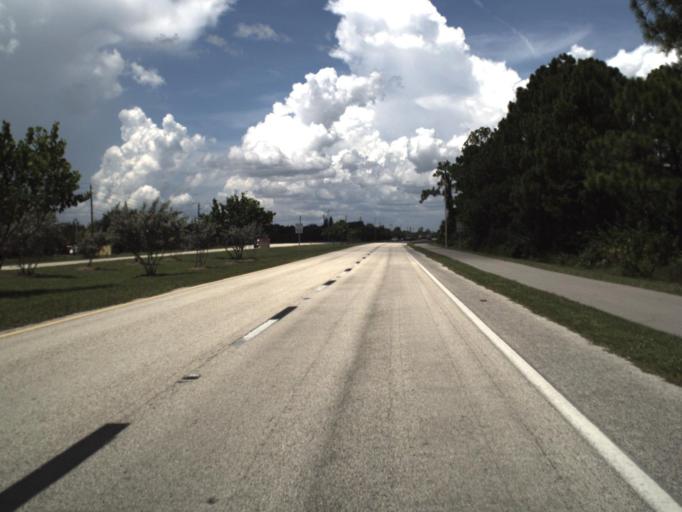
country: US
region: Florida
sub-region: Charlotte County
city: Charlotte Park
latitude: 26.8776
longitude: -82.0100
